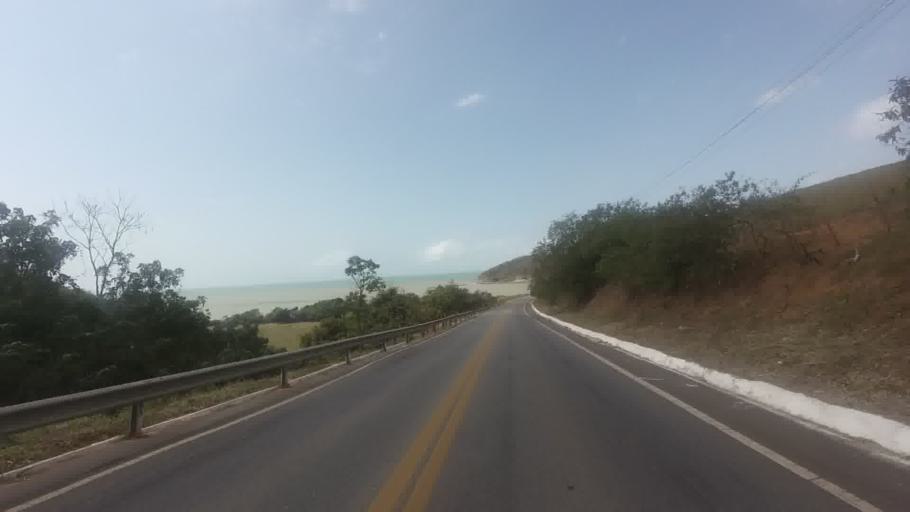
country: BR
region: Espirito Santo
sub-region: Piuma
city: Piuma
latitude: -20.8718
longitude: -40.7629
